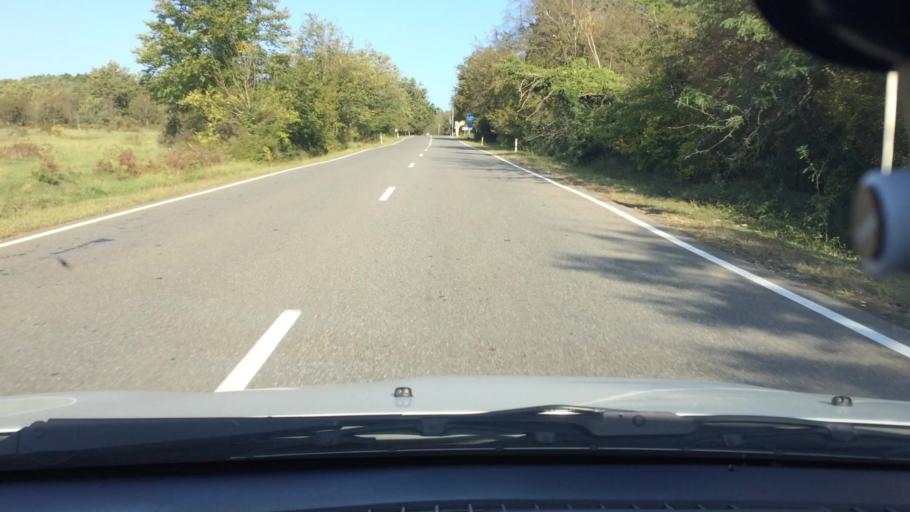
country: GE
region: Imereti
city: Kutaisi
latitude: 42.2444
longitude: 42.7604
